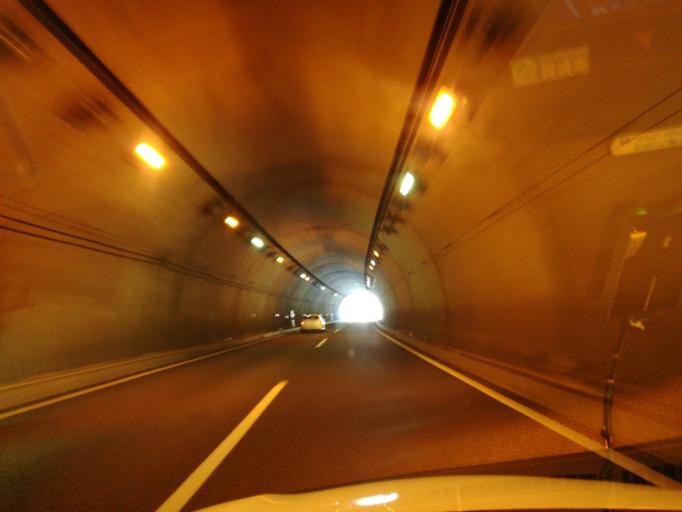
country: JP
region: Ehime
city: Kawanoecho
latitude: 33.8322
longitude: 133.6565
